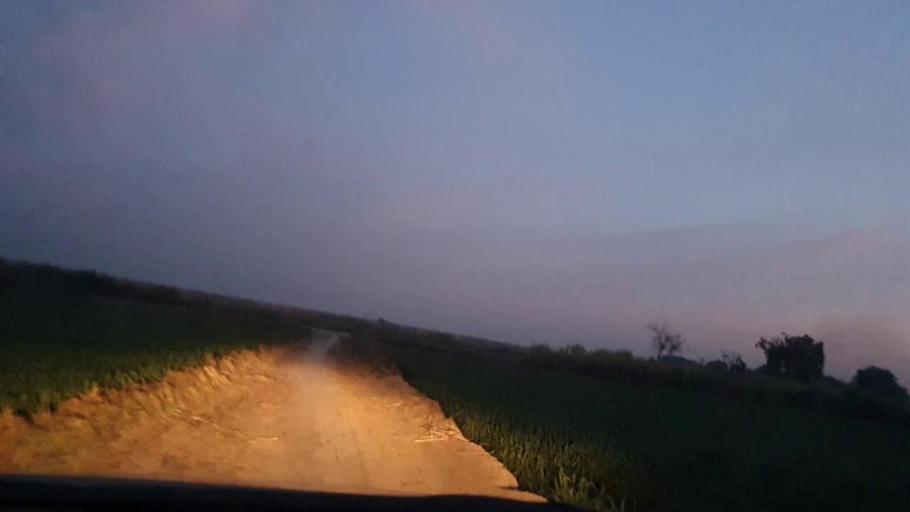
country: PK
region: Sindh
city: Sakrand
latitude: 26.1835
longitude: 68.3062
